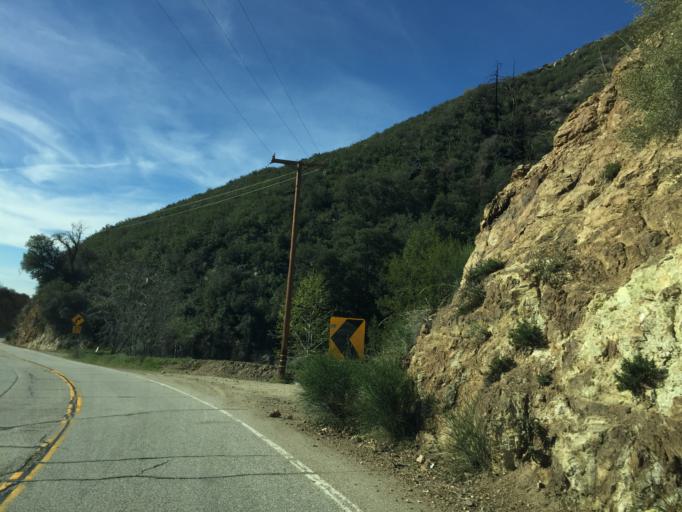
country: US
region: California
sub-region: San Bernardino County
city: San Antonio Heights
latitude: 34.1985
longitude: -117.6771
